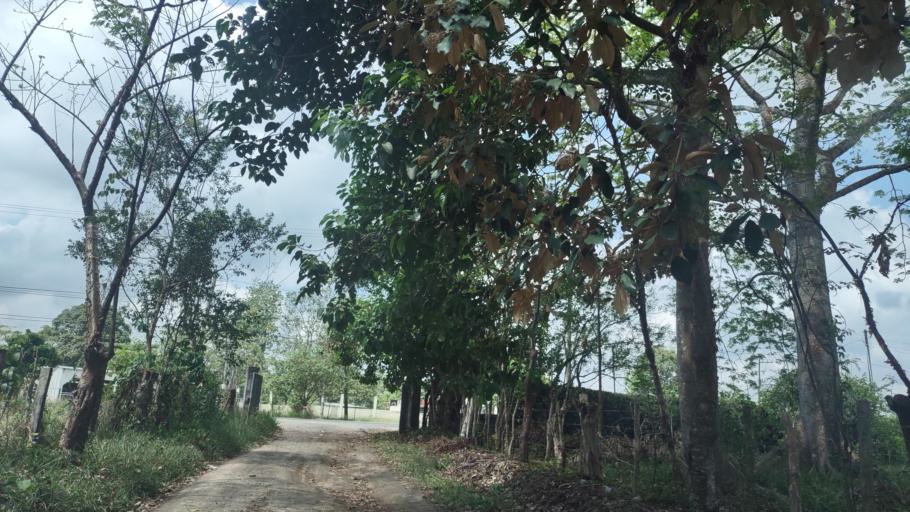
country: MX
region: Veracruz
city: Las Choapas
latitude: 17.9440
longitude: -94.1050
